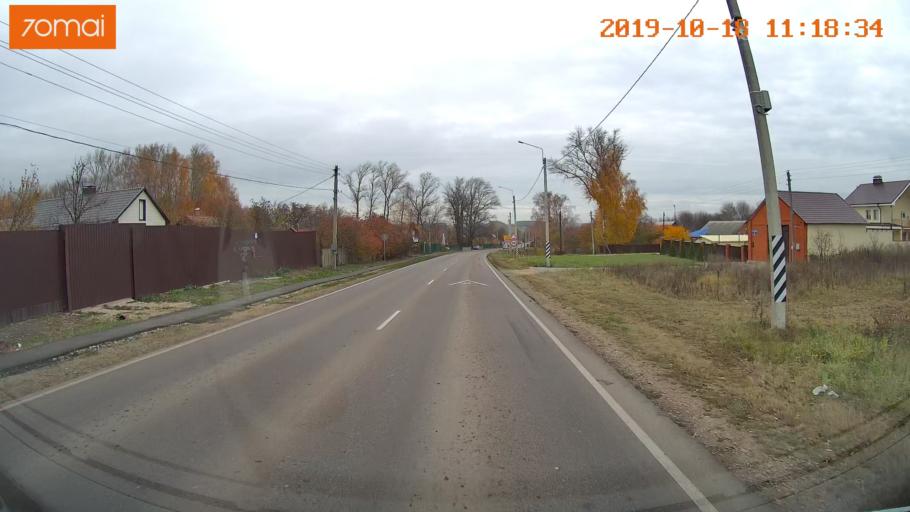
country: RU
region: Tula
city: Kimovsk
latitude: 54.0401
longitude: 38.5505
